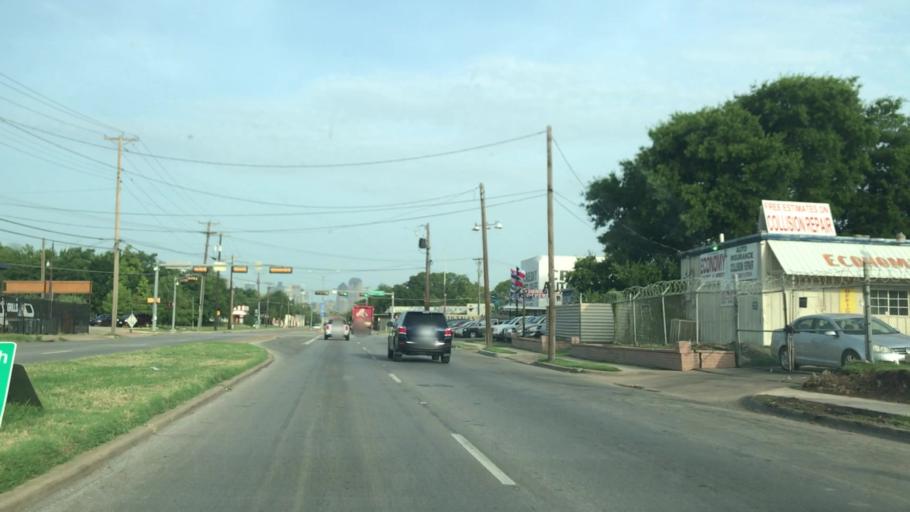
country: US
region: Texas
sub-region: Dallas County
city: Dallas
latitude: 32.7833
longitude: -96.7492
